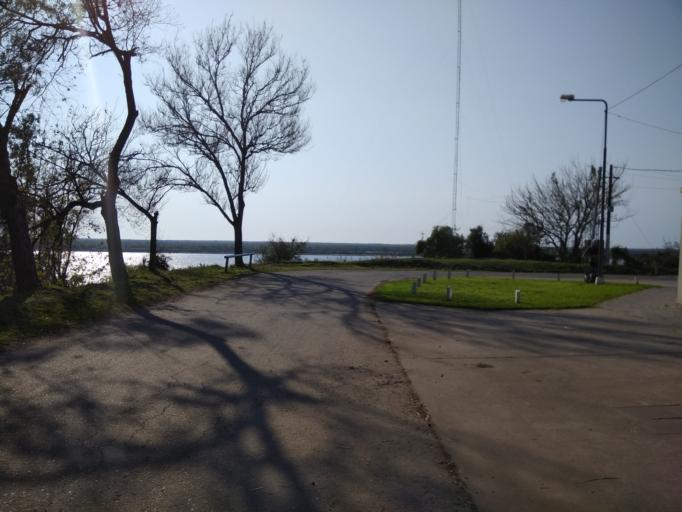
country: AR
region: Santa Fe
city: Granadero Baigorria
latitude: -32.8472
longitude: -60.6973
